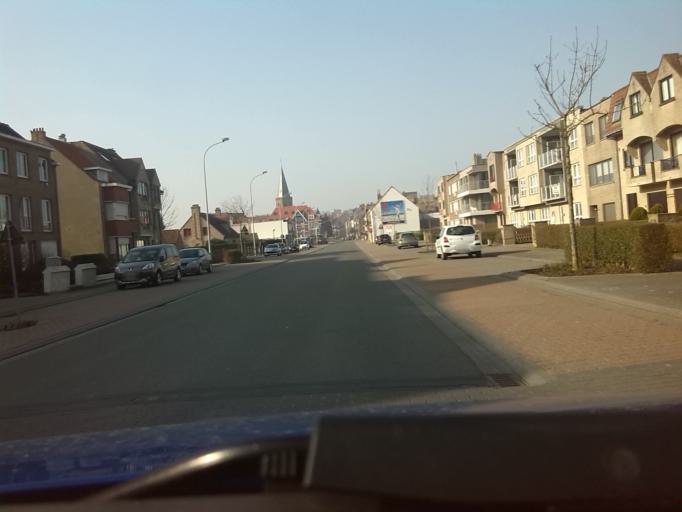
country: BE
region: Flanders
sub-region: Provincie West-Vlaanderen
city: Wenduine
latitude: 51.2956
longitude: 3.0847
